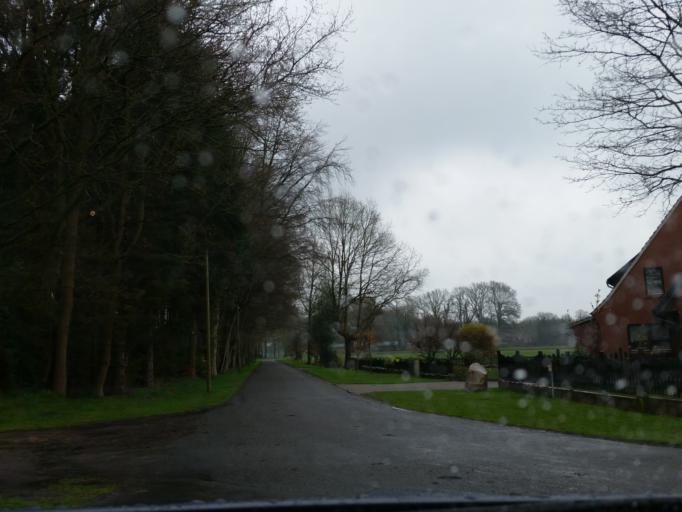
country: DE
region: Lower Saxony
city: Hipstedt
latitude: 53.4771
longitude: 8.9671
